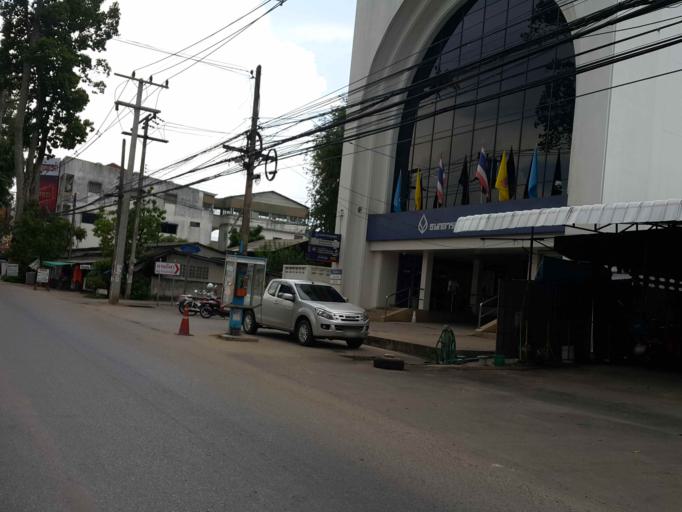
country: TH
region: Chiang Mai
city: Saraphi
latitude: 18.7155
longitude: 99.0332
